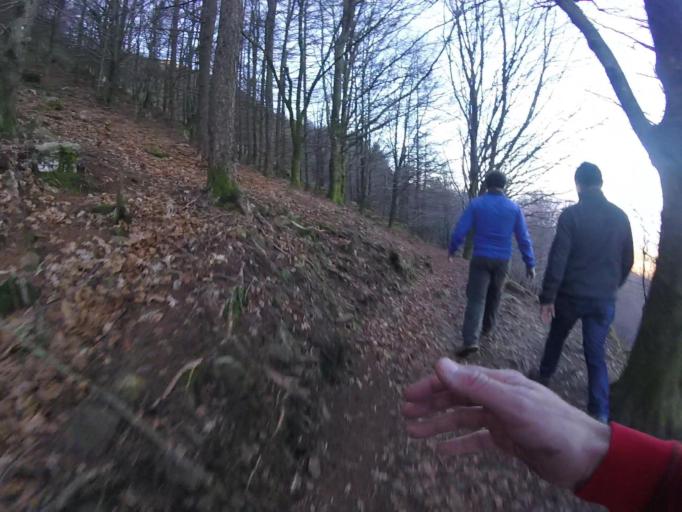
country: ES
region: Basque Country
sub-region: Provincia de Guipuzcoa
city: Irun
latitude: 43.2897
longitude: -1.7838
